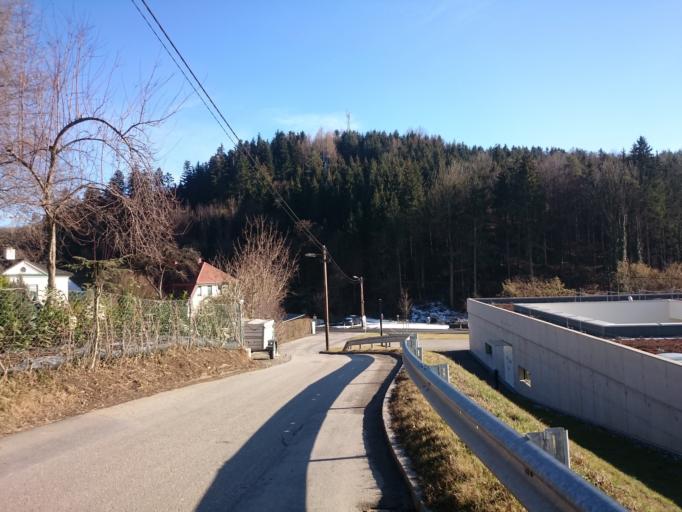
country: AT
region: Styria
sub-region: Graz Stadt
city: Mariatrost
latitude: 47.0884
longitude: 15.4744
